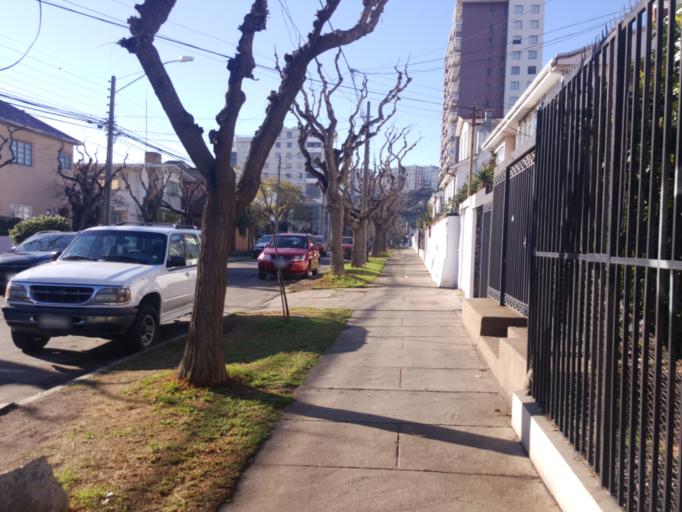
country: CL
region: Valparaiso
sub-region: Provincia de Valparaiso
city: Vina del Mar
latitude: -33.0148
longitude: -71.5473
